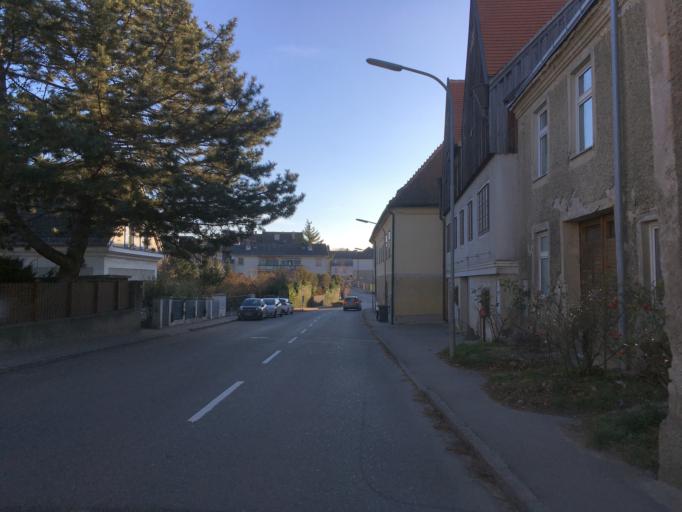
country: AT
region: Lower Austria
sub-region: Politischer Bezirk Wien-Umgebung
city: Klosterneuburg
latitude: 48.3320
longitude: 16.2996
